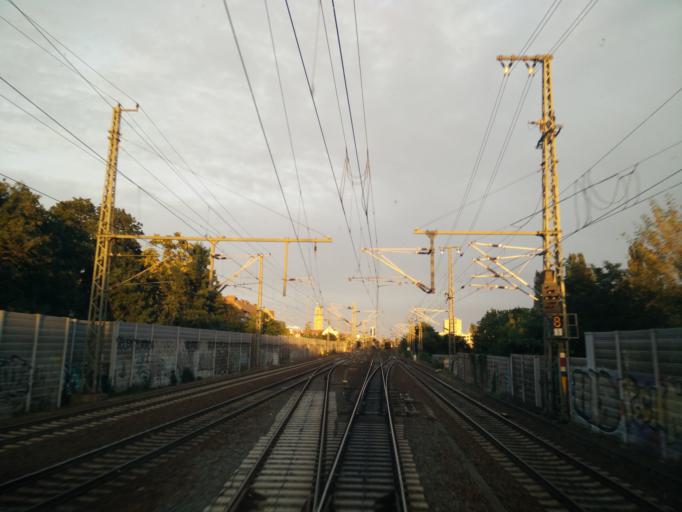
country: DE
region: Berlin
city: Wilhelmstadt
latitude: 52.5364
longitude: 13.1856
